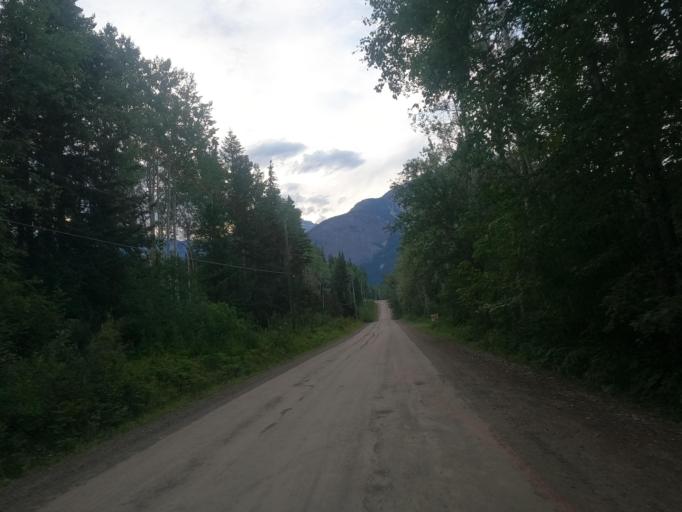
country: CA
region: British Columbia
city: Golden
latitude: 51.4457
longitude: -117.0149
